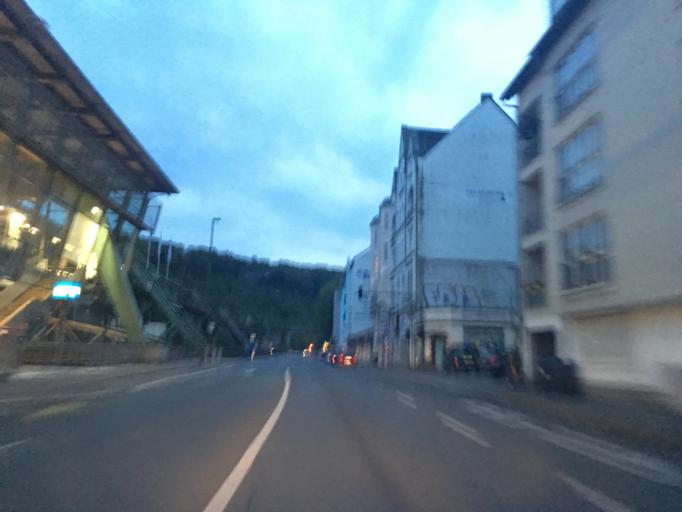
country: DE
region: North Rhine-Westphalia
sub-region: Regierungsbezirk Dusseldorf
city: Solingen
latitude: 51.2412
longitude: 7.1029
